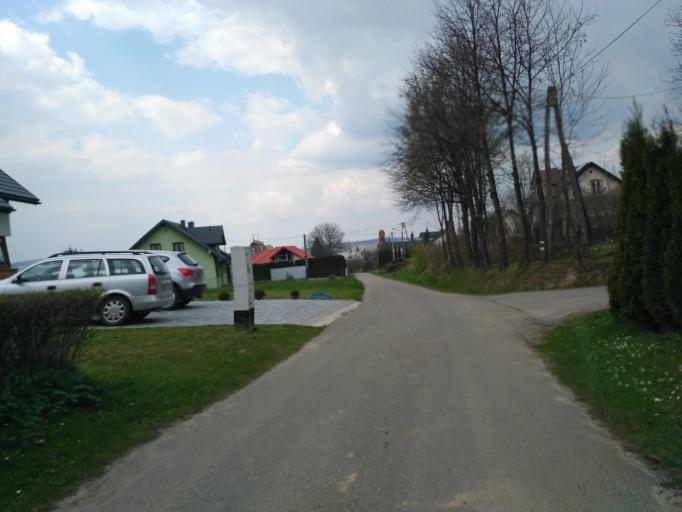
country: PL
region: Subcarpathian Voivodeship
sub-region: Powiat brzozowski
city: Gorki
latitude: 49.6443
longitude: 22.0450
